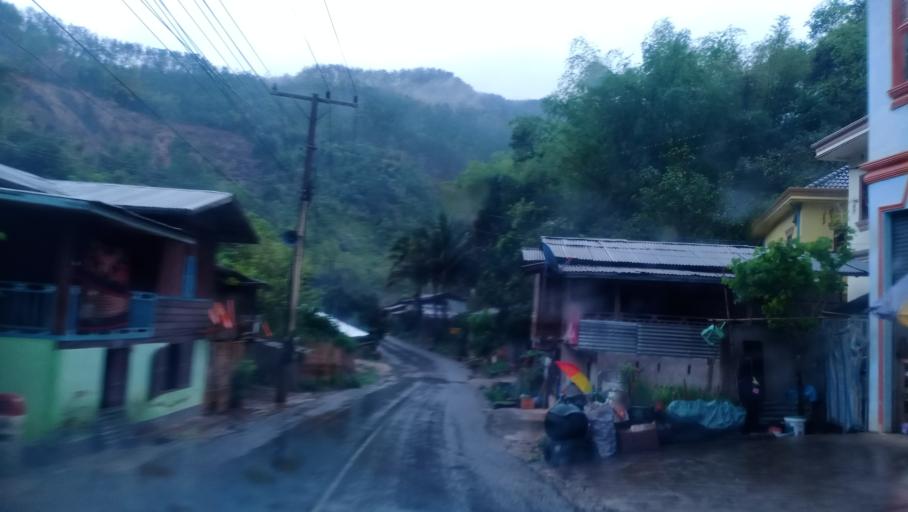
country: LA
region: Phongsali
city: Khoa
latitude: 21.0751
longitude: 102.5025
